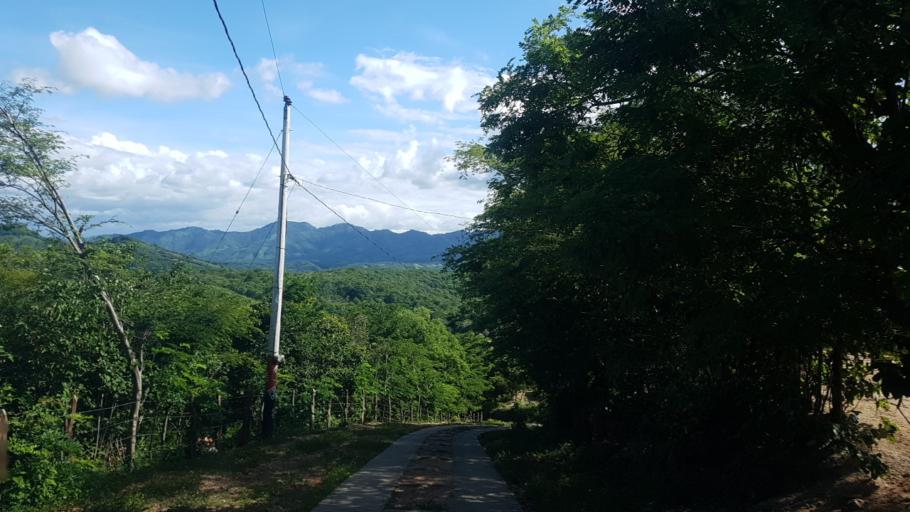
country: NI
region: Nueva Segovia
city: Mozonte
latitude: 13.6450
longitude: -86.3980
